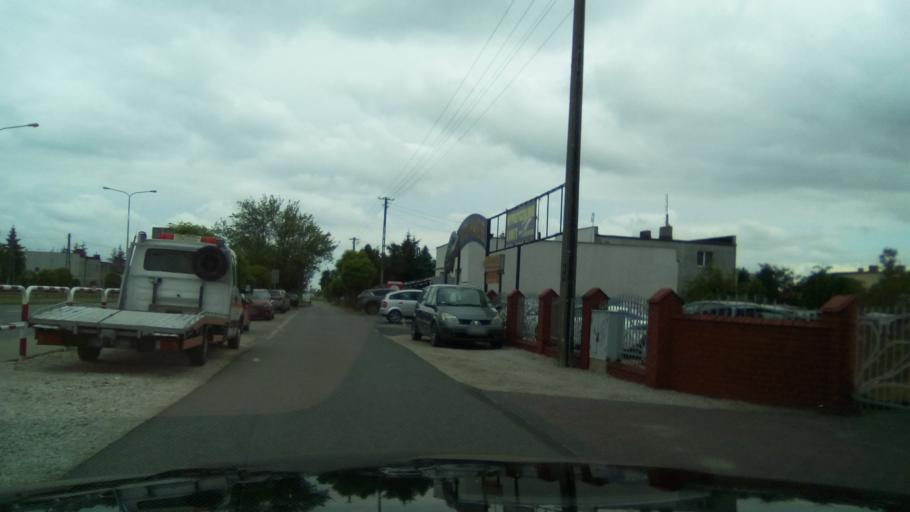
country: PL
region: Greater Poland Voivodeship
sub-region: Powiat gnieznienski
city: Gniezno
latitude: 52.5335
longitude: 17.5635
